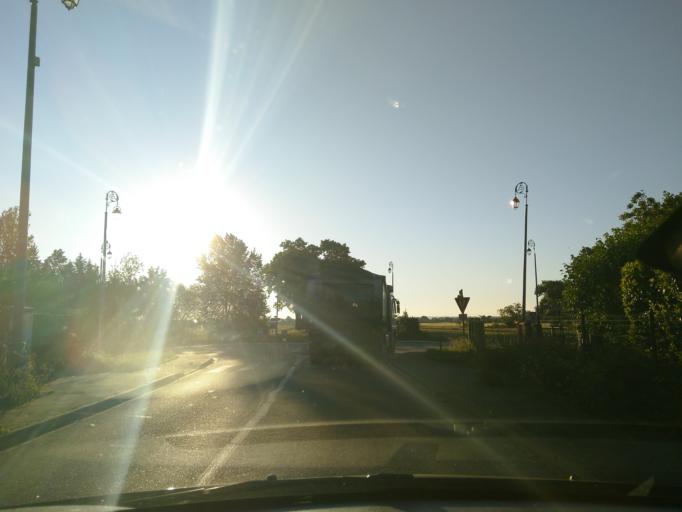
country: FR
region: Midi-Pyrenees
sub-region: Departement de la Haute-Garonne
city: Merville
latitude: 43.7181
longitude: 1.3052
